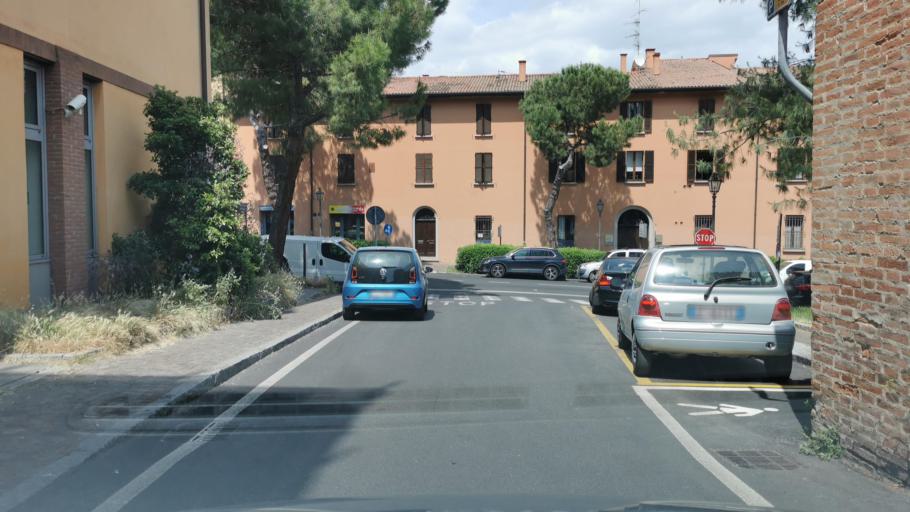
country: IT
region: Emilia-Romagna
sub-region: Provincia di Bologna
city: Castel San Pietro Terme
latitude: 44.3988
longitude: 11.5910
